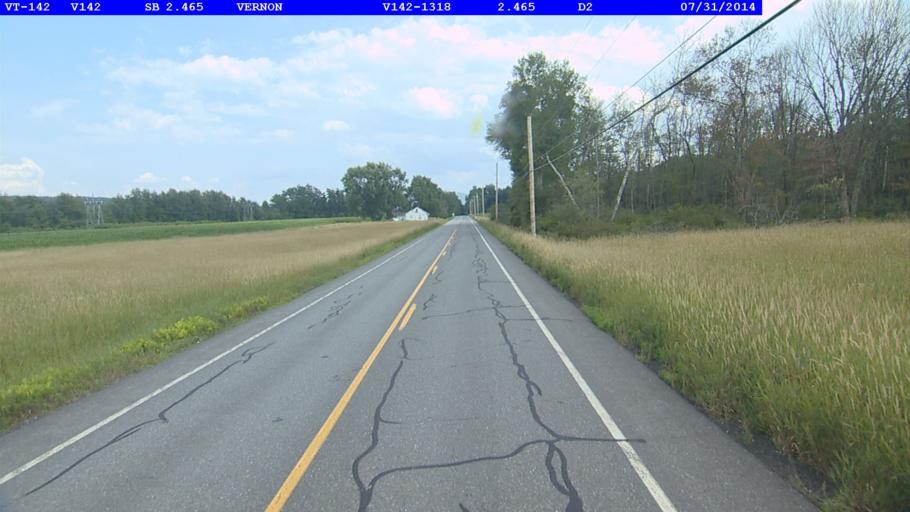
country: US
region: New Hampshire
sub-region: Cheshire County
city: Hinsdale
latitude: 42.7571
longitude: -72.4880
